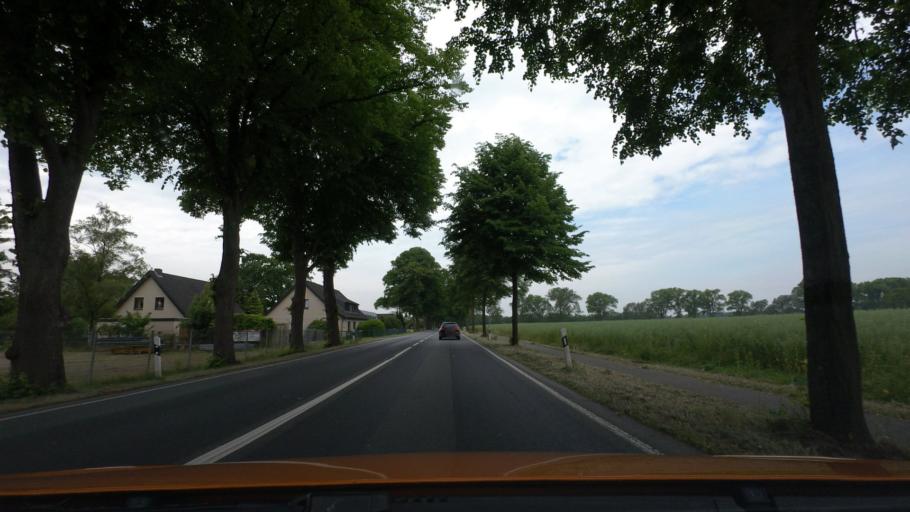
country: DE
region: Lower Saxony
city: Stuhr
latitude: 52.9961
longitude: 8.7475
